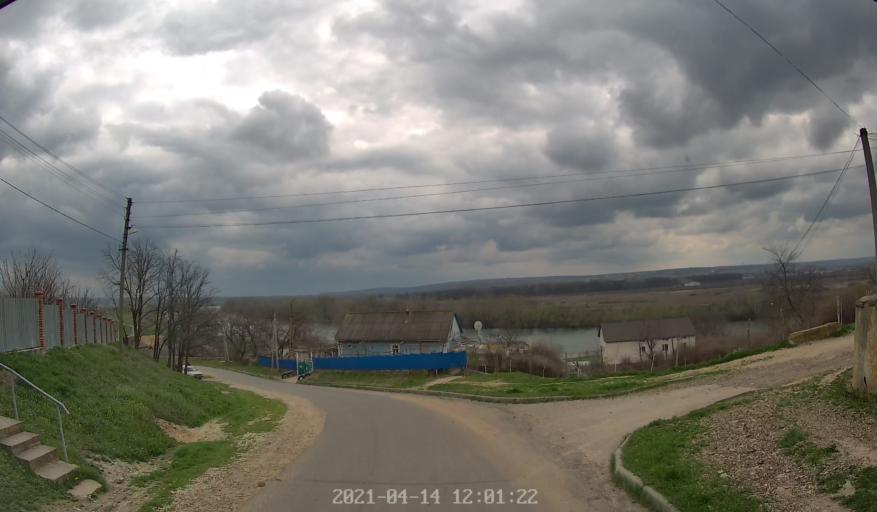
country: MD
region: Criuleni
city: Criuleni
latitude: 47.1657
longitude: 29.1987
